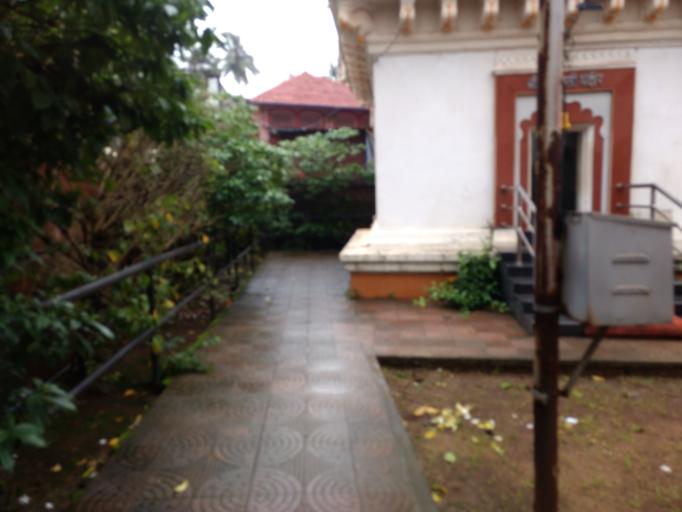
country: IN
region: Maharashtra
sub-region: Ratnagiri
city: Guhagar
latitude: 17.4836
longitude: 73.1903
